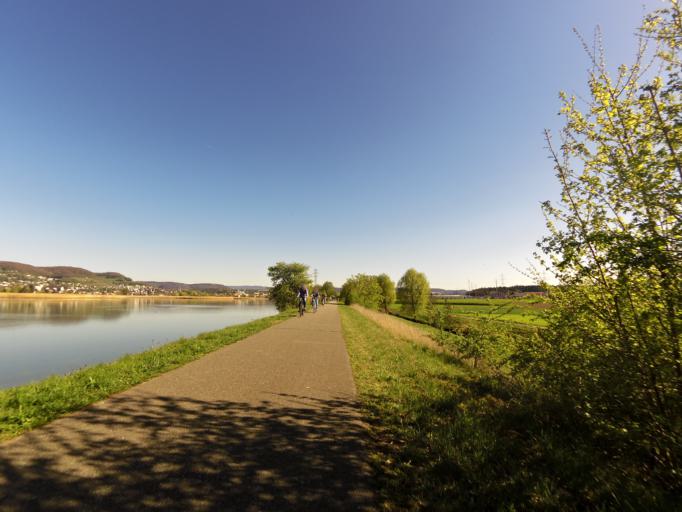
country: CH
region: Aargau
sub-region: Bezirk Zurzach
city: Klingnau
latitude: 47.5832
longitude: 8.2332
